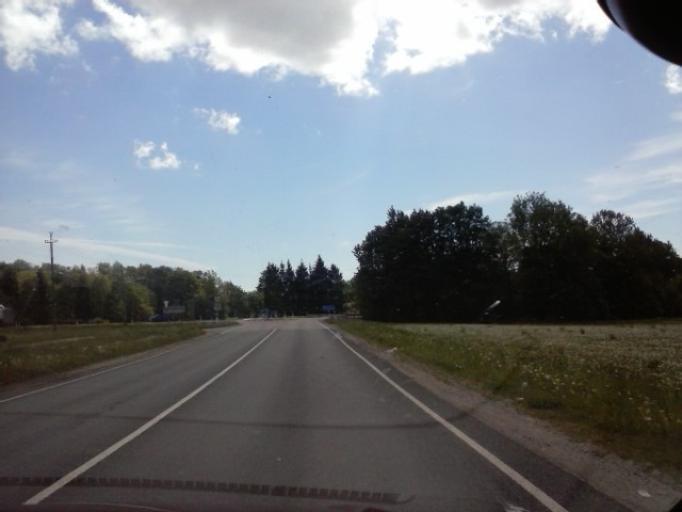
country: EE
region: Laeaene
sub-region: Ridala Parish
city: Uuemoisa
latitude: 58.9578
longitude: 23.7826
